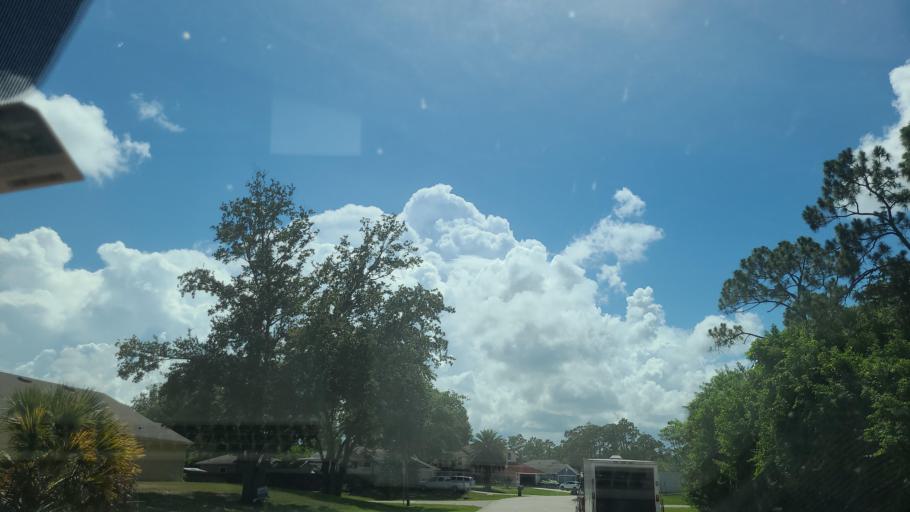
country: US
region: Florida
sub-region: Indian River County
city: Sebastian
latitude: 27.7633
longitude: -80.4960
